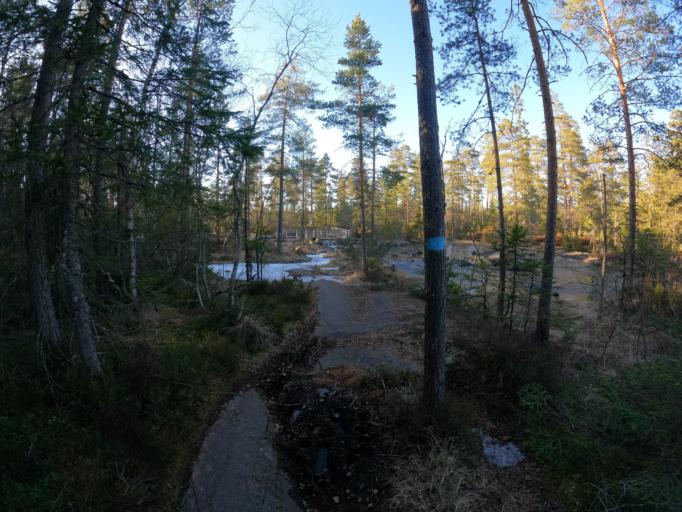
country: NO
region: Akershus
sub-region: Nittedal
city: Aneby
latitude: 60.1069
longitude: 10.9399
